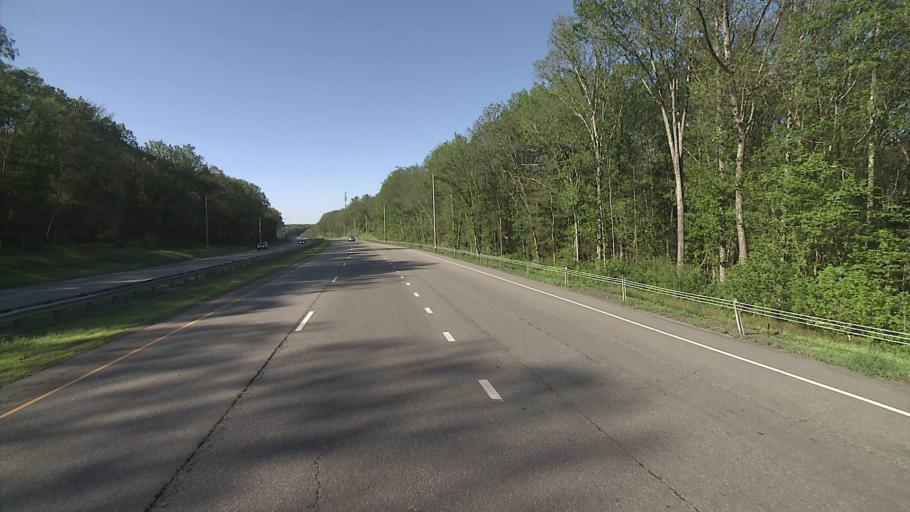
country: US
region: Connecticut
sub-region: Windham County
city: Wauregan
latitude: 41.7515
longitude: -71.8790
